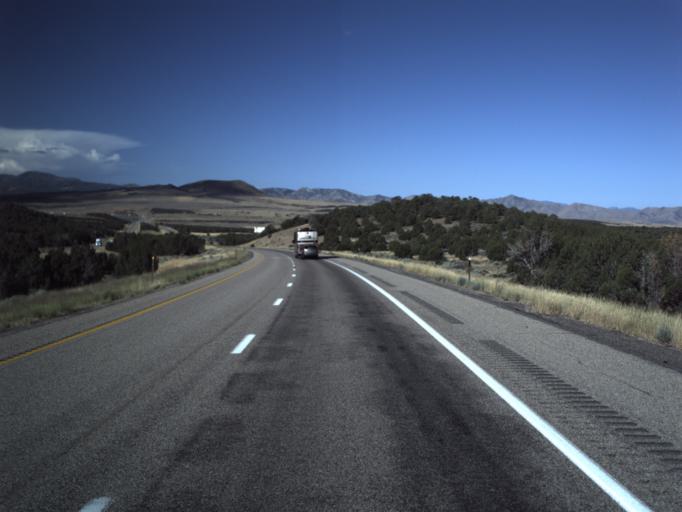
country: US
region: Utah
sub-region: Beaver County
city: Beaver
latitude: 38.6044
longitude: -112.5501
